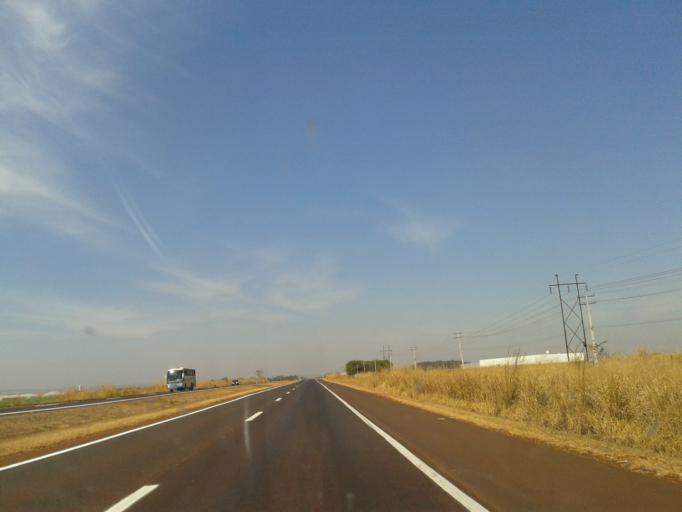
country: BR
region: Goias
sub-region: Itumbiara
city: Itumbiara
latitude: -18.3319
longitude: -49.2253
